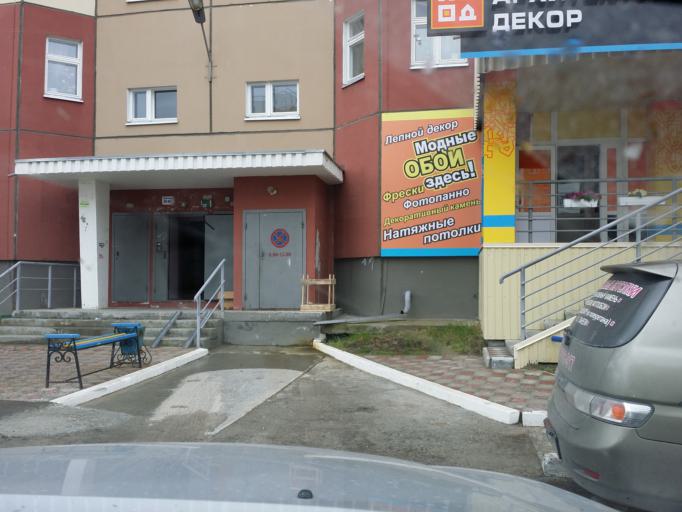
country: RU
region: Khanty-Mansiyskiy Avtonomnyy Okrug
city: Nizhnevartovsk
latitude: 60.9322
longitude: 76.6202
